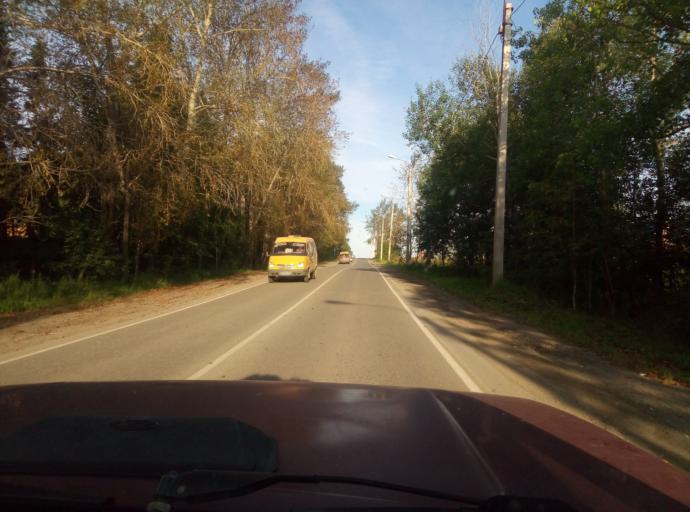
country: RU
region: Sverdlovsk
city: Krasnotur'insk
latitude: 59.7574
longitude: 60.1556
